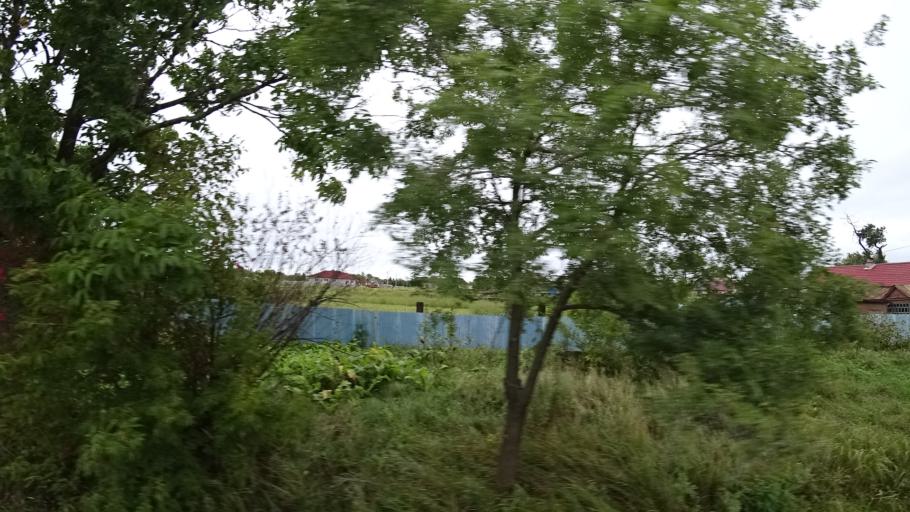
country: RU
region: Primorskiy
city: Chernigovka
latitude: 44.3410
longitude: 132.5481
